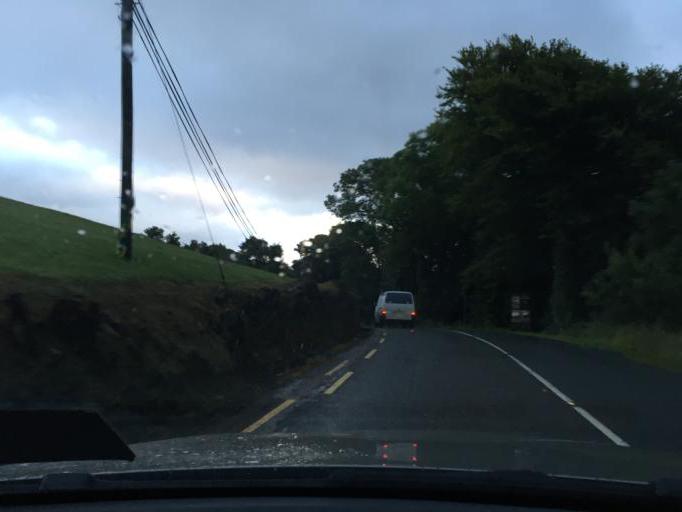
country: IE
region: Ulster
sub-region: County Donegal
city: Killybegs
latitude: 54.6388
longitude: -8.4831
